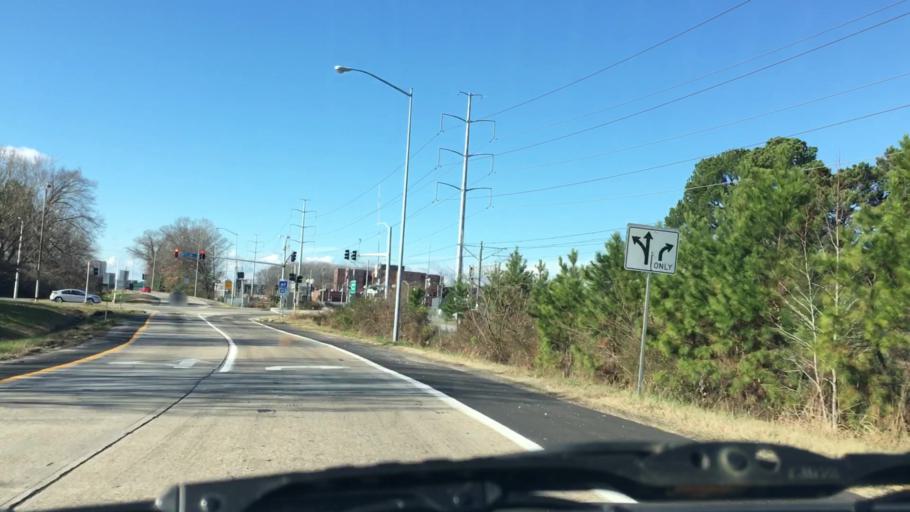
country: US
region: Virginia
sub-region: City of Norfolk
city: Norfolk
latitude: 36.8460
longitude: -76.2516
